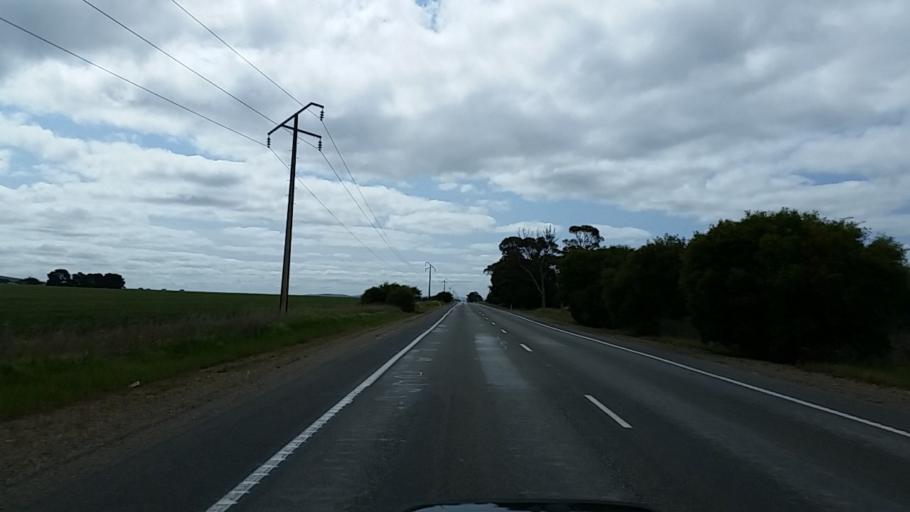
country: AU
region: South Australia
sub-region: Port Pirie City and Dists
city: Crystal Brook
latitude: -33.5913
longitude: 138.2246
